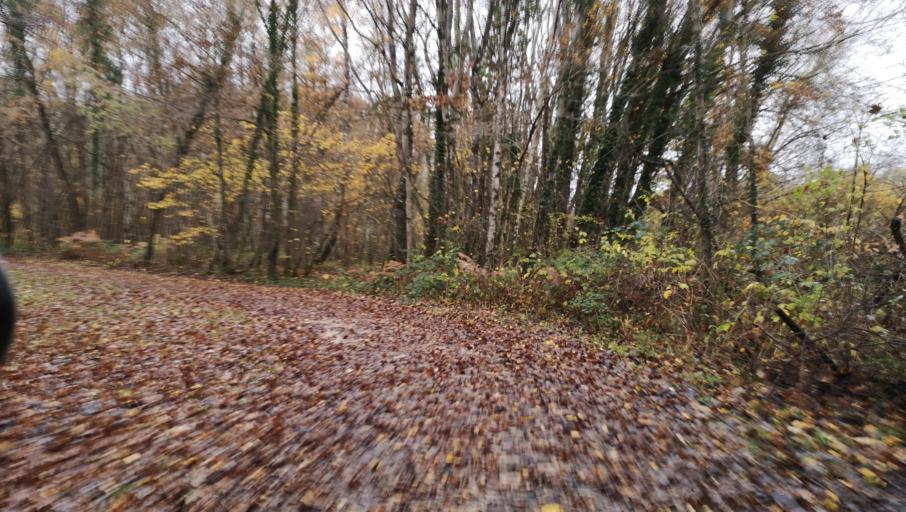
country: FR
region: Centre
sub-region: Departement du Loiret
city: Boigny-sur-Bionne
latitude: 47.9418
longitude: 2.0008
